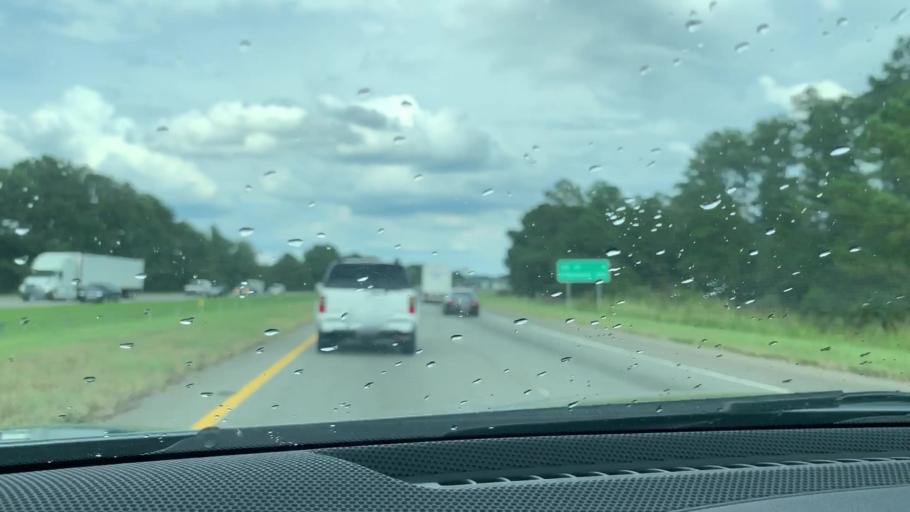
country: US
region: South Carolina
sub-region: Hampton County
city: Yemassee
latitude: 32.5916
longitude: -80.9204
